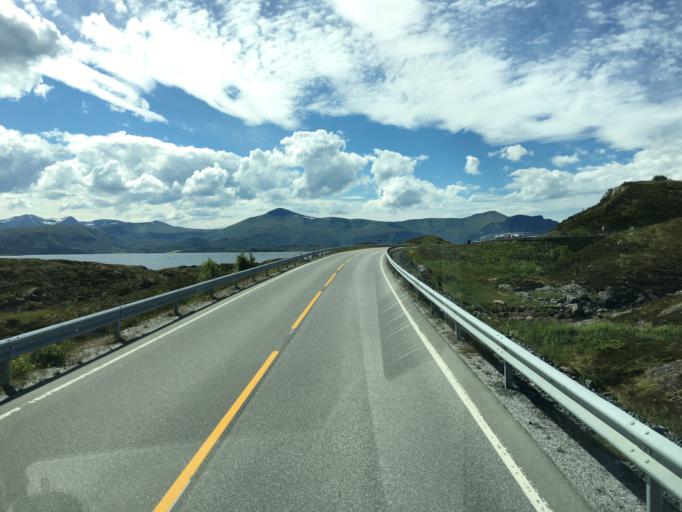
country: NO
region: More og Romsdal
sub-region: Eide
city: Eide
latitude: 63.0195
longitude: 7.3691
